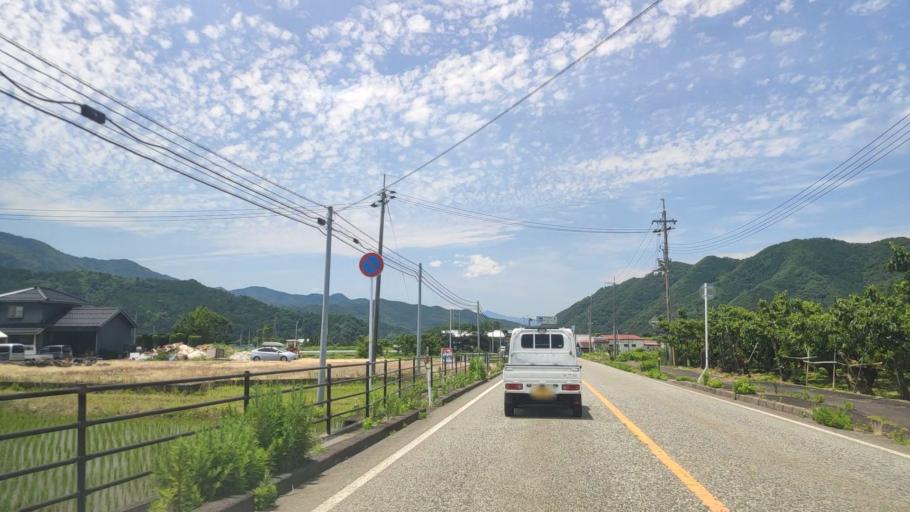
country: JP
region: Tottori
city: Tottori
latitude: 35.3623
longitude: 134.3504
